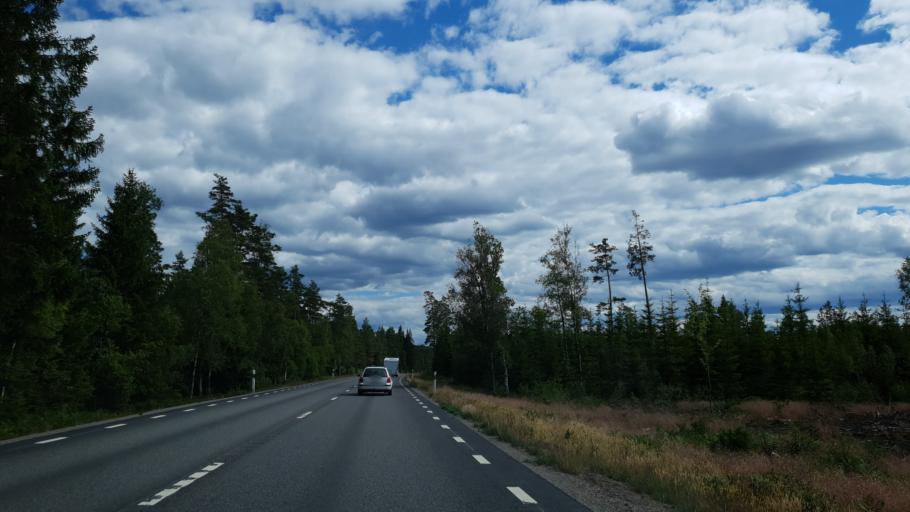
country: SE
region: Kronoberg
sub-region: Lessebo Kommun
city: Lessebo
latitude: 56.8275
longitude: 15.4013
